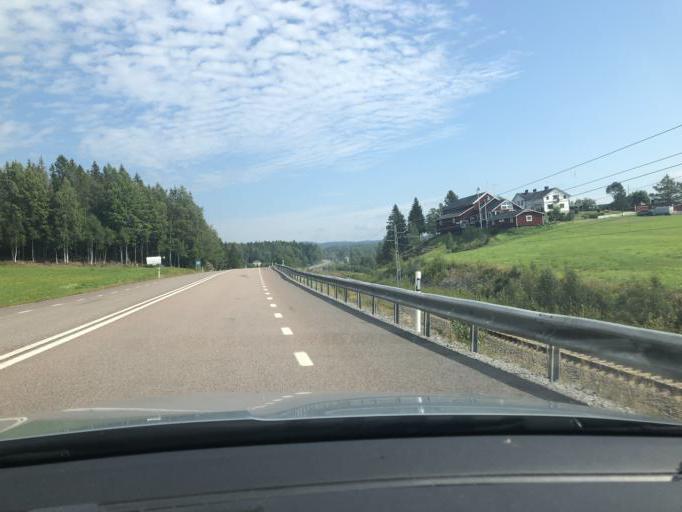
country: SE
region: Vaesternorrland
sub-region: Kramfors Kommun
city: Kramfors
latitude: 62.8275
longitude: 17.8500
